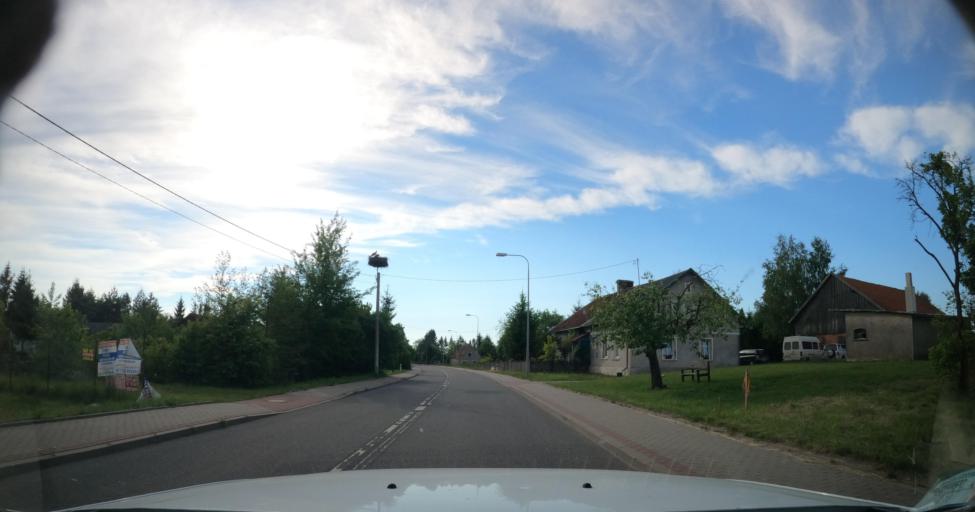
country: PL
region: Warmian-Masurian Voivodeship
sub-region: Powiat ostrodzki
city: Morag
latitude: 54.0808
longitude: 19.9009
